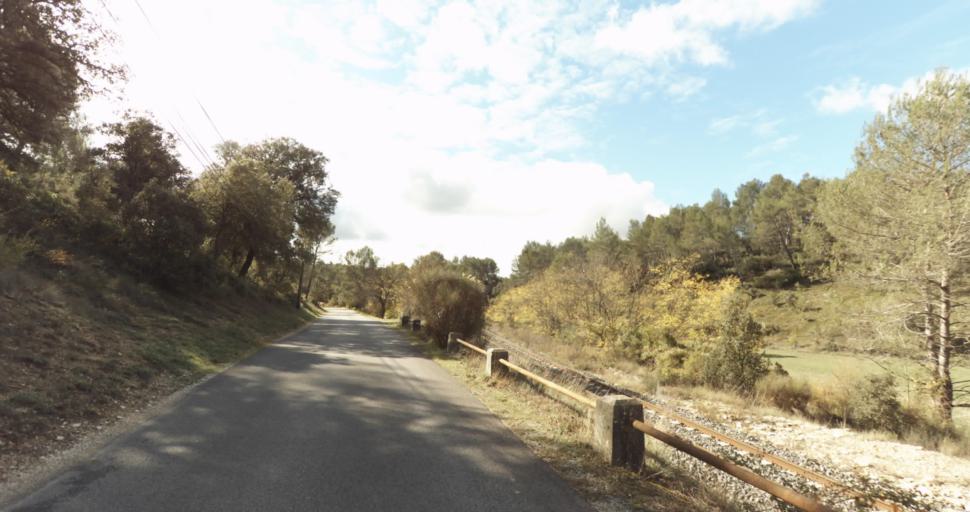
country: FR
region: Provence-Alpes-Cote d'Azur
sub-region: Departement des Bouches-du-Rhone
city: Venelles
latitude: 43.5879
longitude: 5.5079
